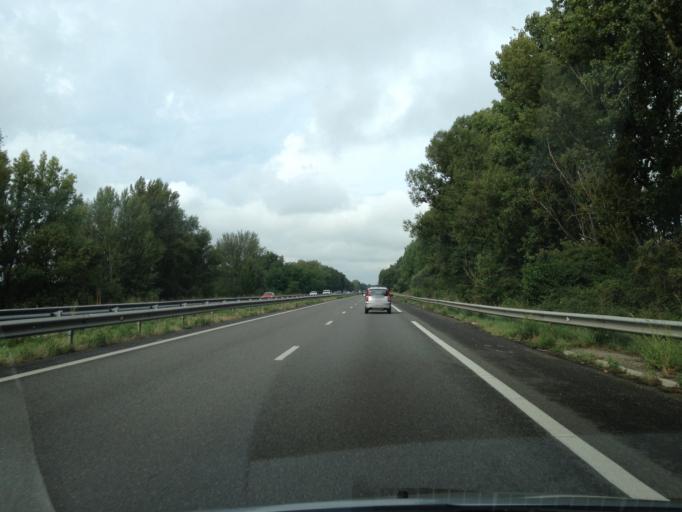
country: FR
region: Midi-Pyrenees
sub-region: Departement du Tarn-et-Garonne
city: Castelsarrasin
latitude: 44.0440
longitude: 1.0623
